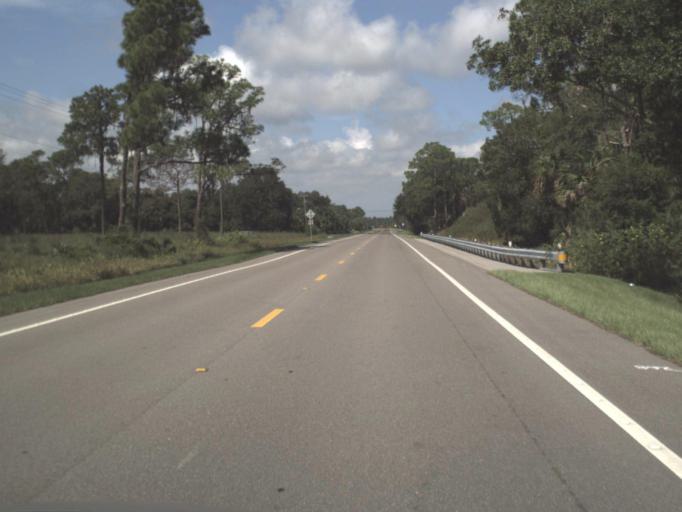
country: US
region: Florida
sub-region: Sarasota County
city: Lake Sarasota
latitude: 27.2443
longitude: -82.3478
